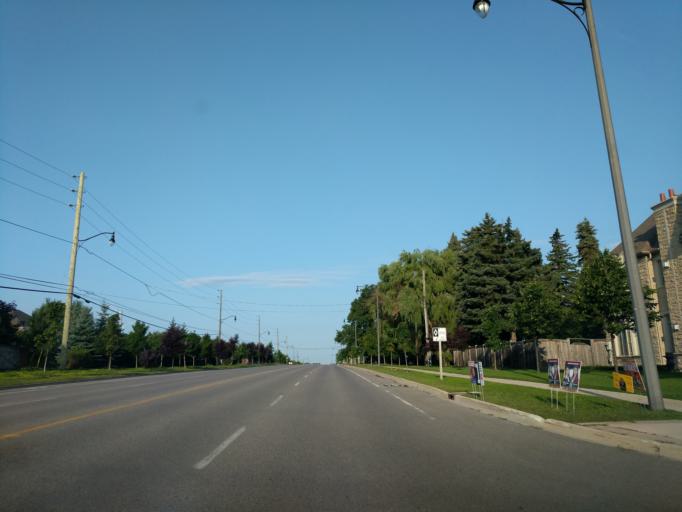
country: CA
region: Ontario
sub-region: York
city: Richmond Hill
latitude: 43.9097
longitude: -79.4372
